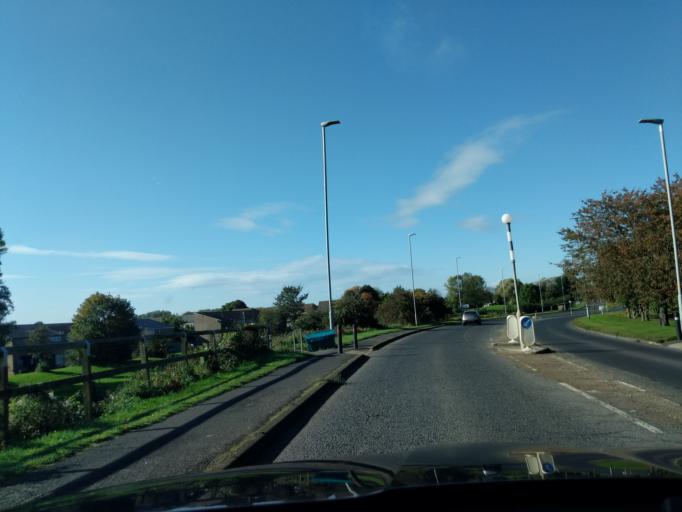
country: GB
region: England
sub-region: Northumberland
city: Cramlington
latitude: 55.0872
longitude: -1.5990
